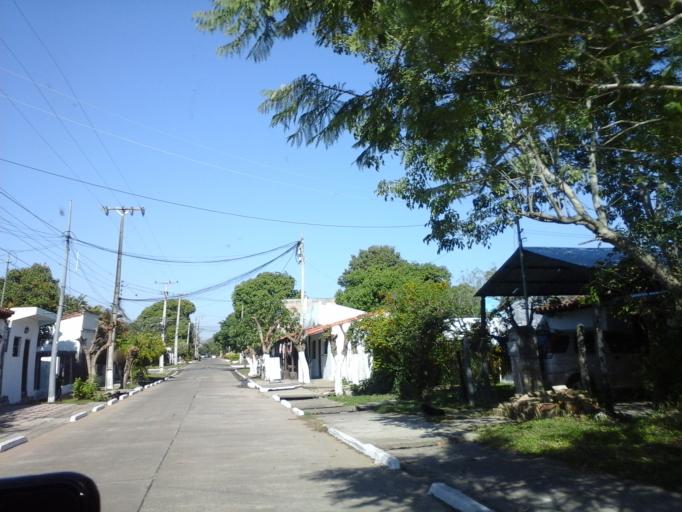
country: PY
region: Neembucu
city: Pilar
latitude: -26.8593
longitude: -58.3081
